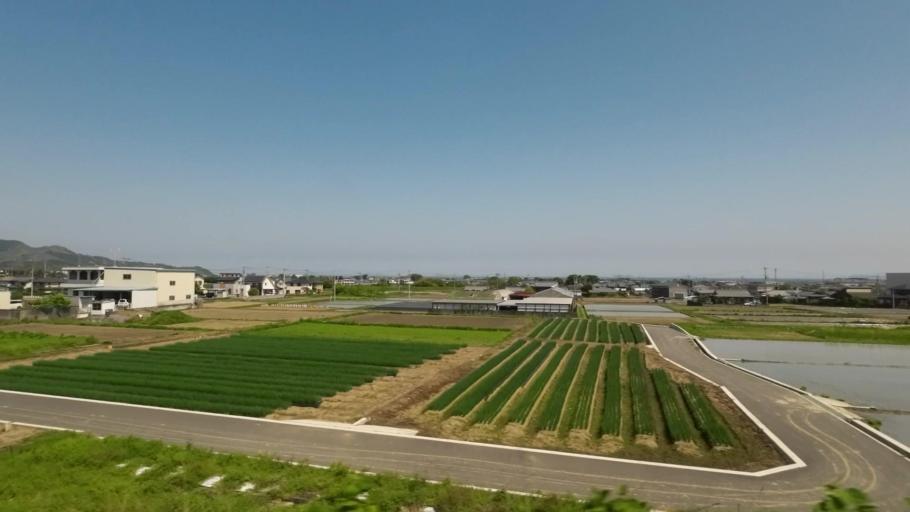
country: JP
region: Ehime
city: Niihama
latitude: 33.9626
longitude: 133.4420
